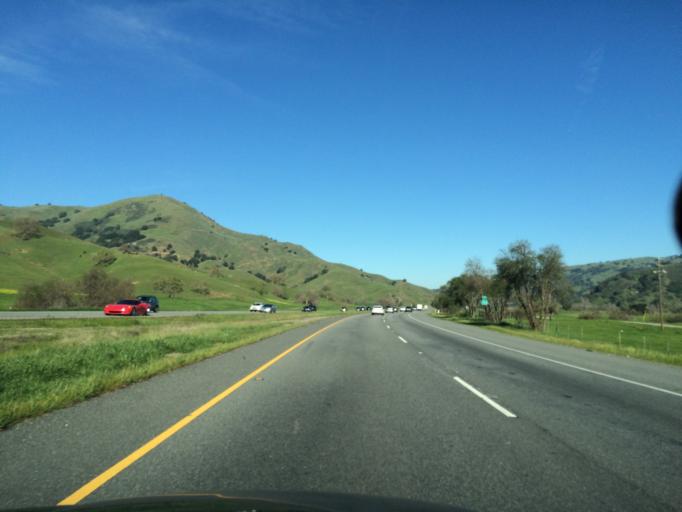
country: US
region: California
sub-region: San Benito County
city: Hollister
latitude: 37.0051
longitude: -121.3682
